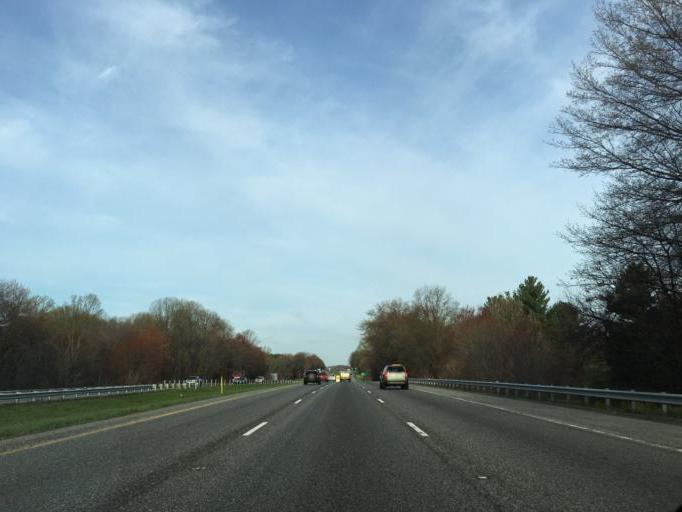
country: US
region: Maryland
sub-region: Carroll County
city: Sykesville
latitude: 39.3067
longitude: -76.9313
